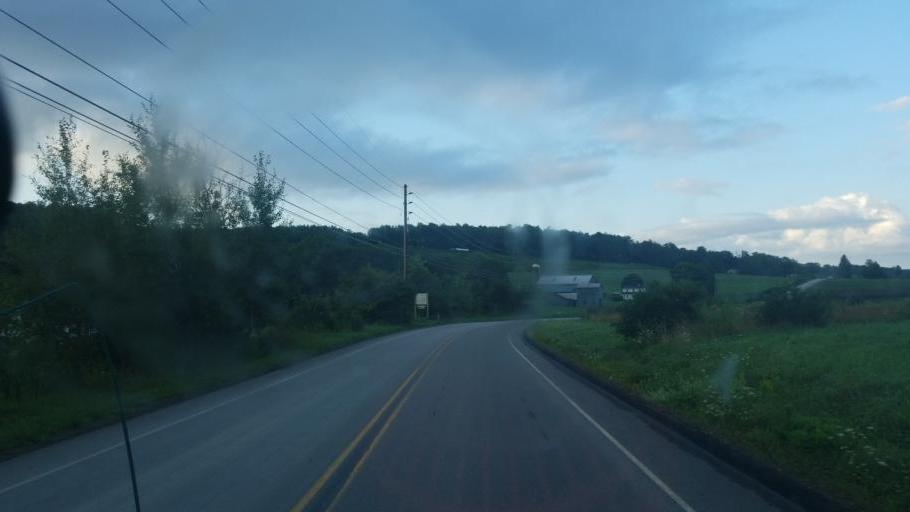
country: US
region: Pennsylvania
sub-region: Potter County
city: Galeton
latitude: 41.8569
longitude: -77.7670
